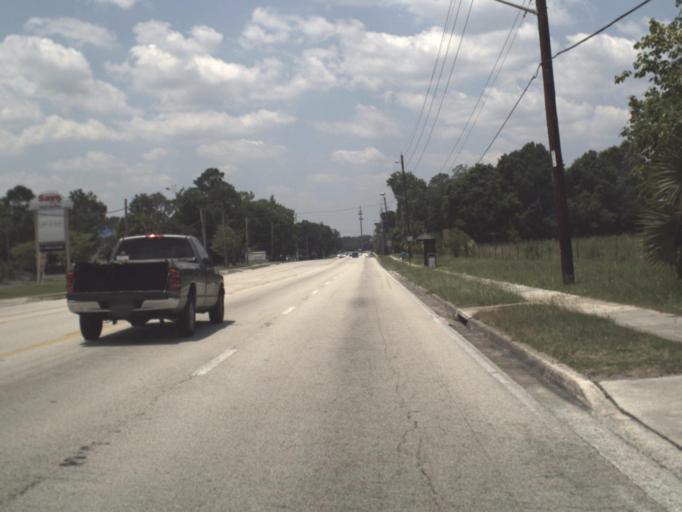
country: US
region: Florida
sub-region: Duval County
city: Jacksonville
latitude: 30.3742
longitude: -81.7157
